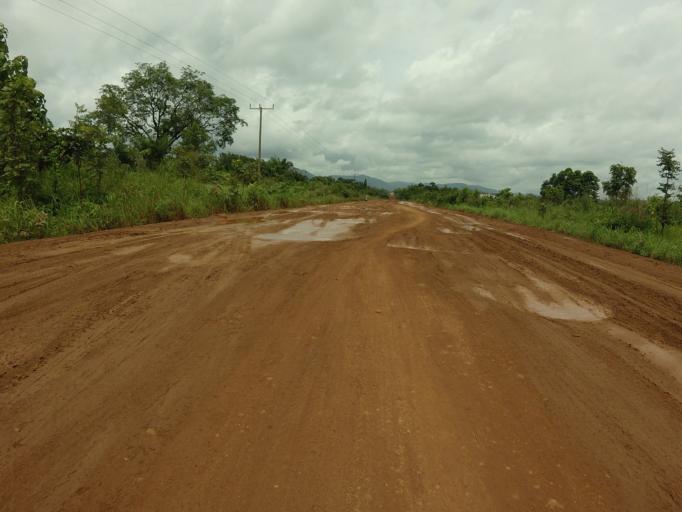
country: GH
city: Kpandae
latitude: 8.2818
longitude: 0.5038
